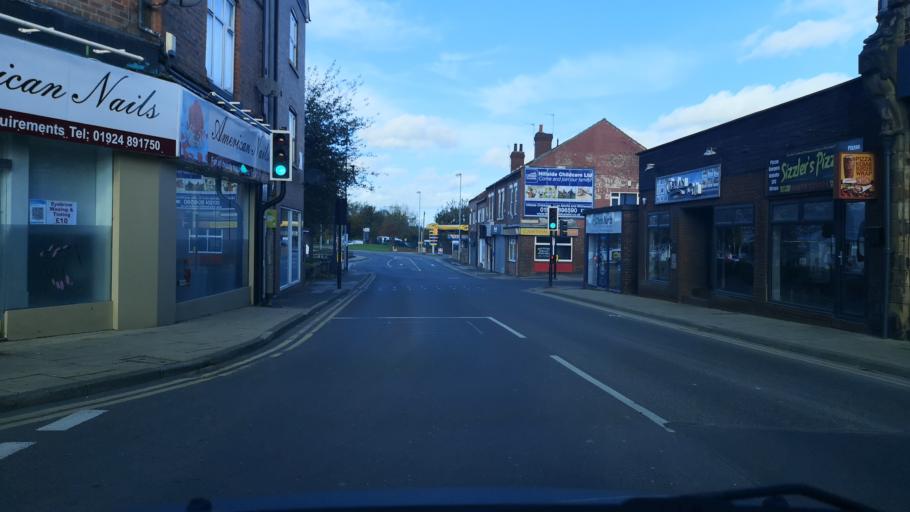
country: GB
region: England
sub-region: City and Borough of Wakefield
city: Normanton
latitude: 53.7000
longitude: -1.4209
